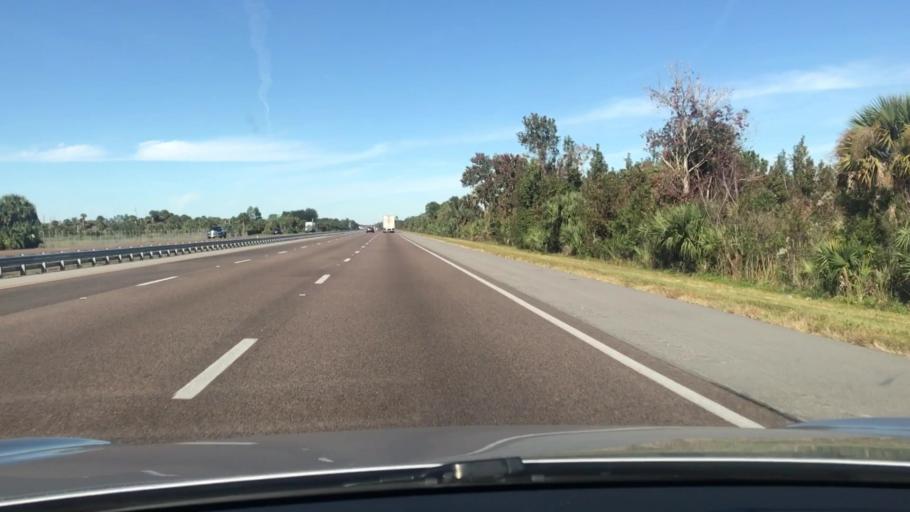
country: US
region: Florida
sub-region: Volusia County
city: Oak Hill
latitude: 28.8001
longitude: -80.9018
